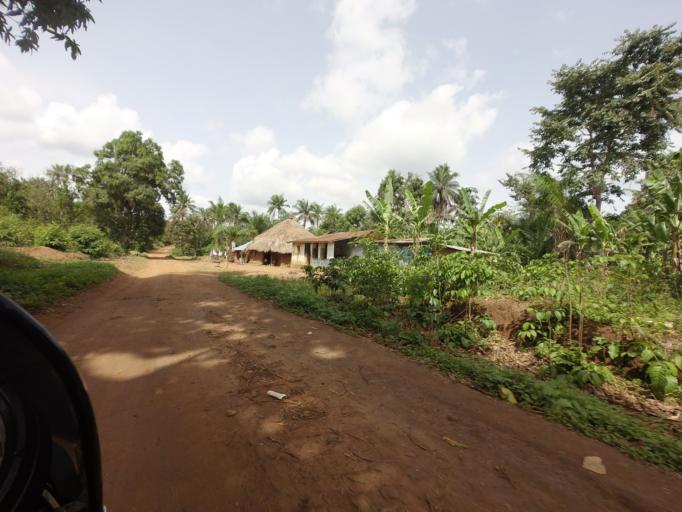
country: SL
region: Northern Province
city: Kambia
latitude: 9.1041
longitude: -12.9661
